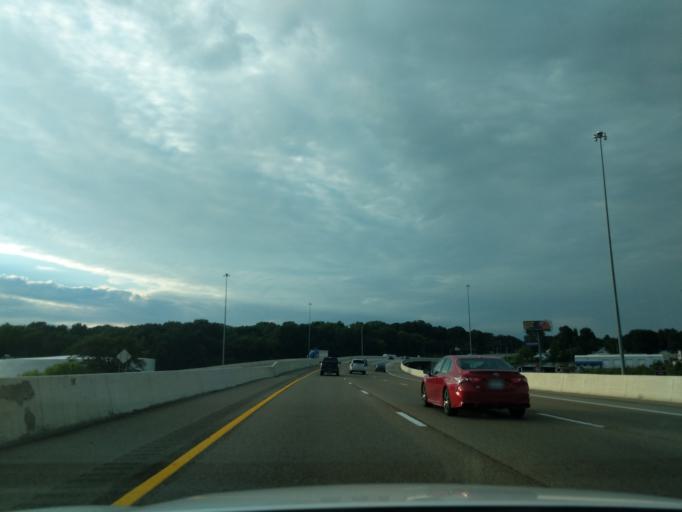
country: US
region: Tennessee
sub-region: Shelby County
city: New South Memphis
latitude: 35.0853
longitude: -90.0757
